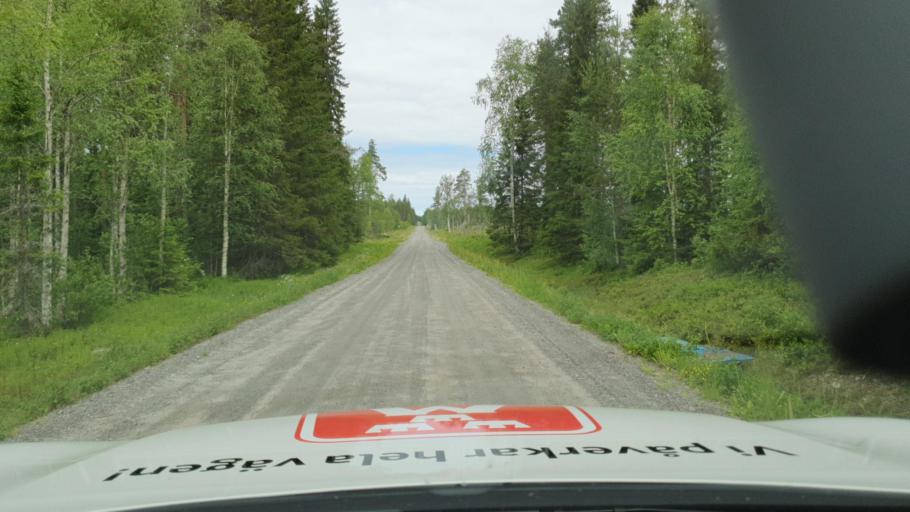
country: SE
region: Vaesterbotten
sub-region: Skelleftea Kommun
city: Burtraesk
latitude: 64.4452
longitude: 20.3084
